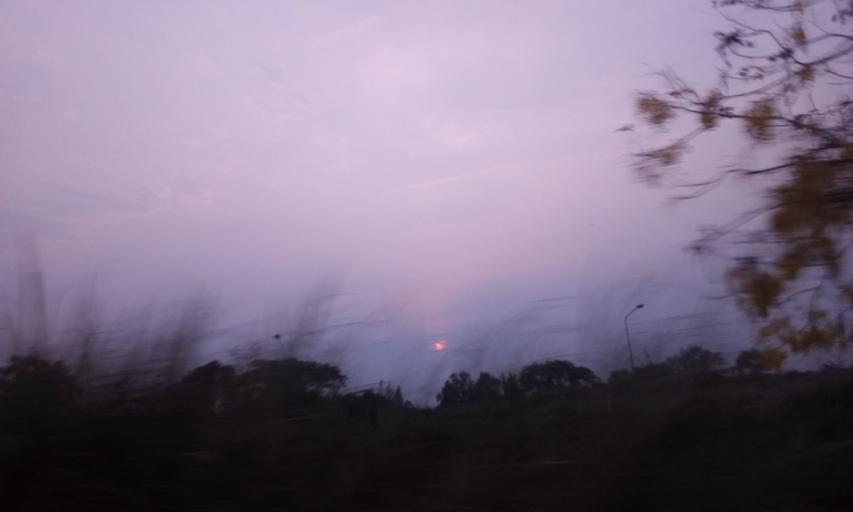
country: TH
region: Pathum Thani
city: Nong Suea
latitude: 14.0611
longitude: 100.8929
